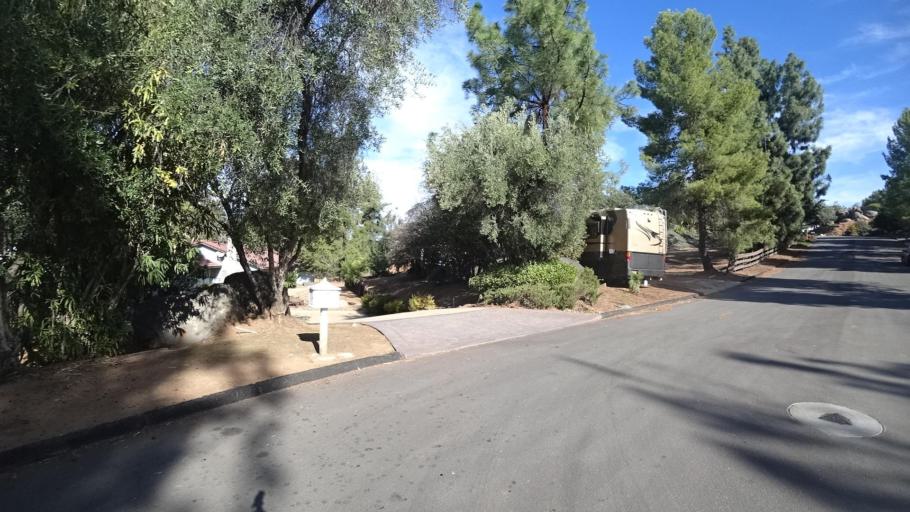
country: US
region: California
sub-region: San Diego County
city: Alpine
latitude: 32.8136
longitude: -116.7748
